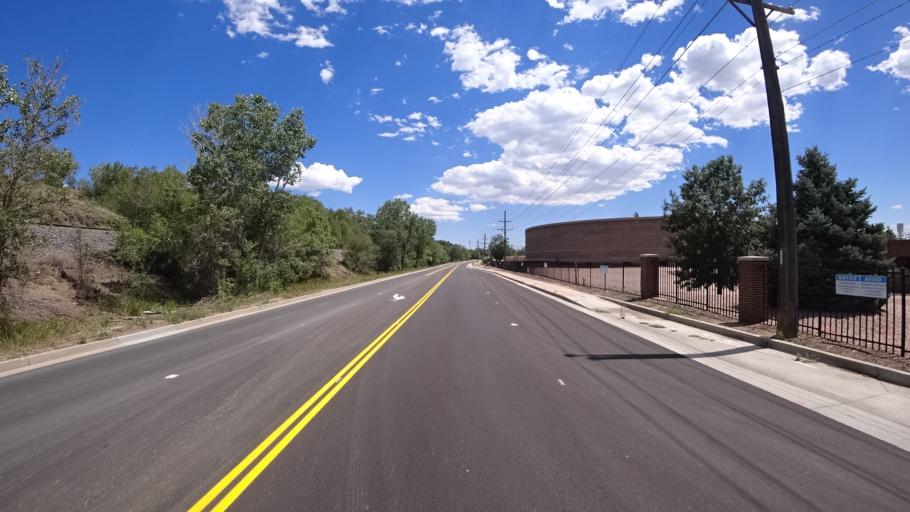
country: US
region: Colorado
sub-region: El Paso County
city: Colorado Springs
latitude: 38.8145
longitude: -104.8077
